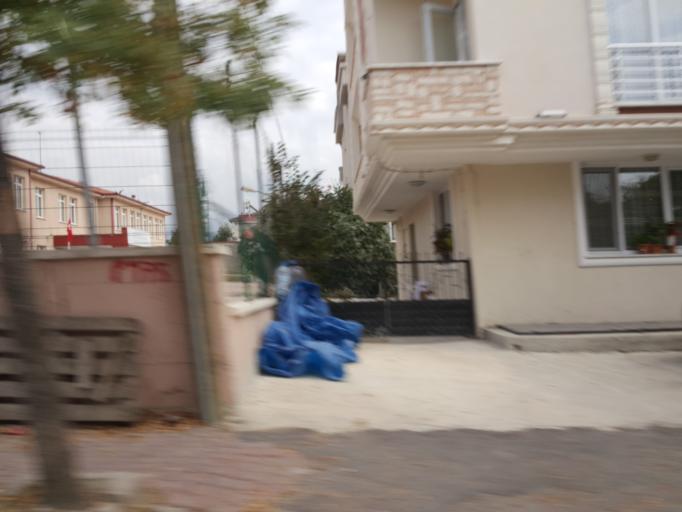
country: TR
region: Sinop
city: Duragan
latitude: 41.4229
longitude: 35.0540
